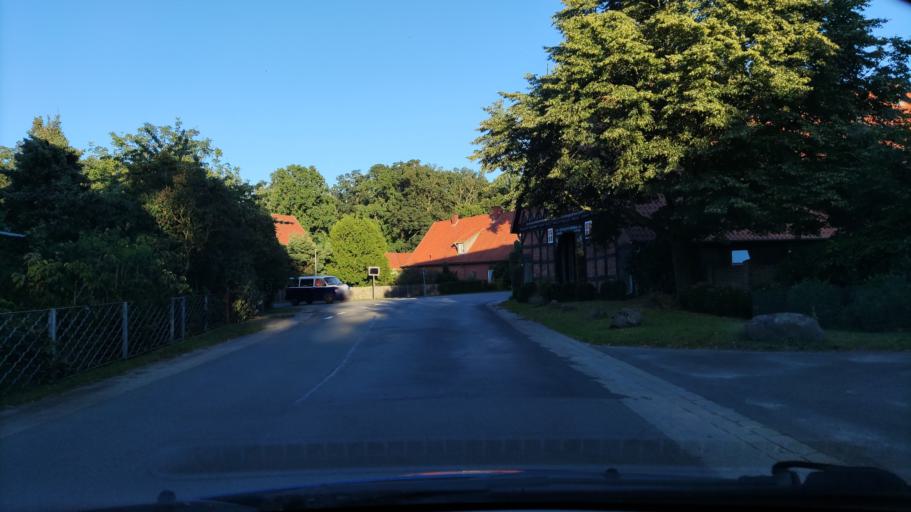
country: DE
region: Lower Saxony
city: Luechow
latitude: 53.0001
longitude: 11.1514
